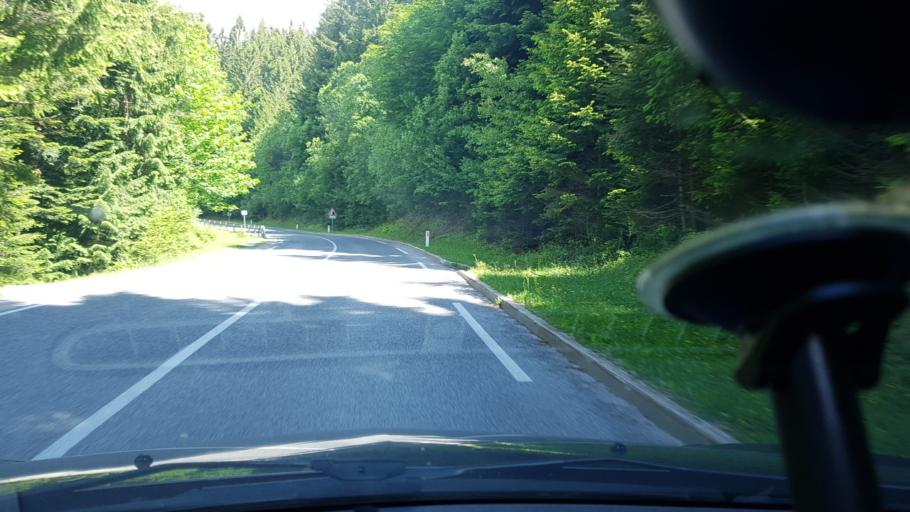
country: SI
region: Zrece
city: Zrece
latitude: 46.4351
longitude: 15.3686
